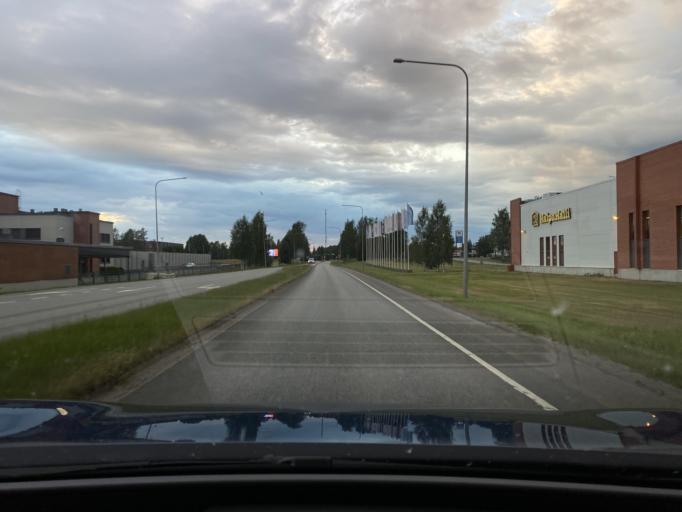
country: FI
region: Northern Ostrobothnia
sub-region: Raahe
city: Raahe
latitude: 64.6736
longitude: 24.4840
